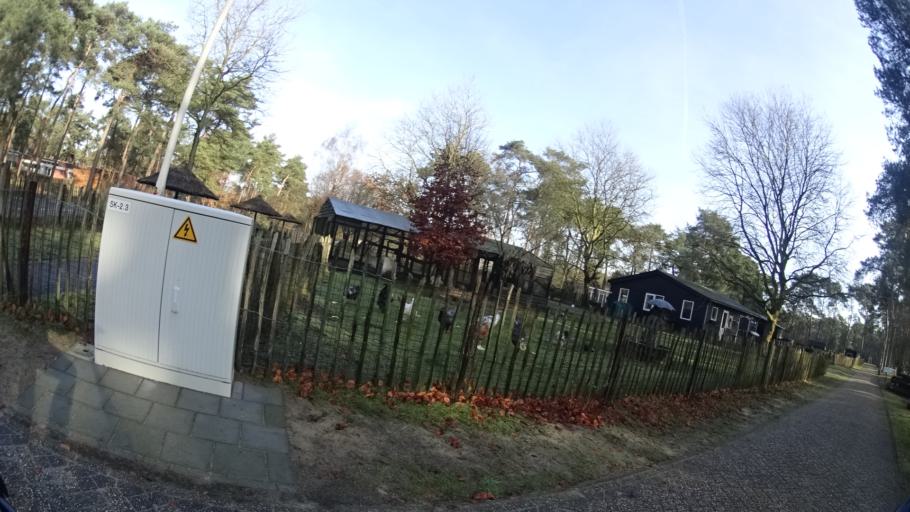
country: NL
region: Gelderland
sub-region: Gemeente Ede
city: Wekerom
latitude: 52.0893
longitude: 5.7343
